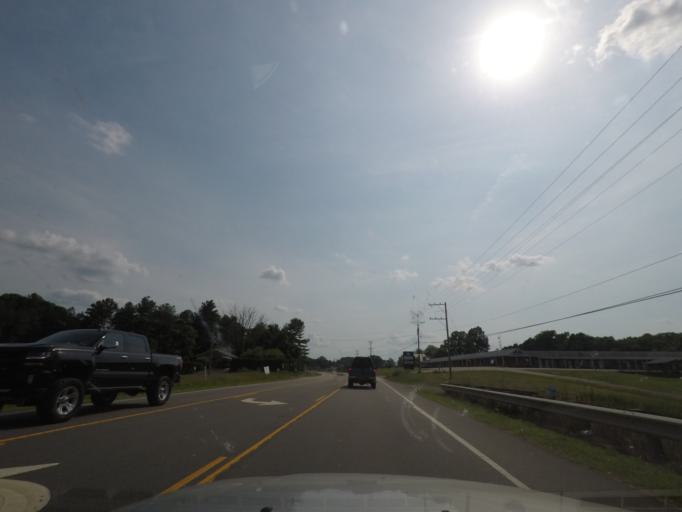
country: US
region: Virginia
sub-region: Buckingham County
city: Buckingham
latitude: 37.5318
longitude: -78.4883
